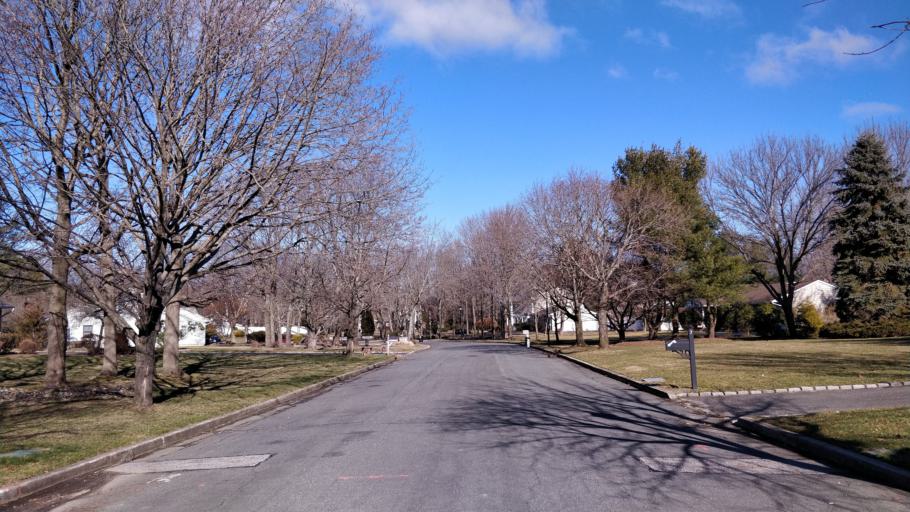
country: US
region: New York
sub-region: Suffolk County
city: Saint James
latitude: 40.8835
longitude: -73.1387
